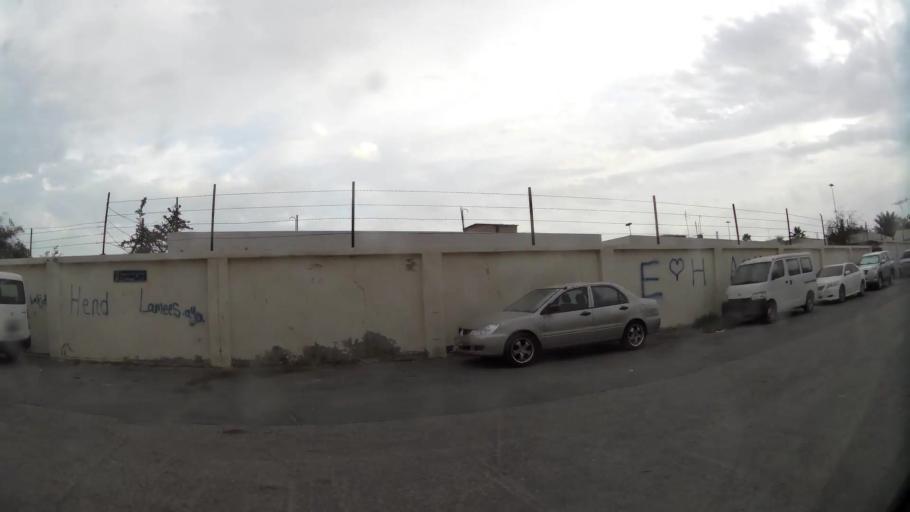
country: QA
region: Baladiyat ad Dawhah
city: Doha
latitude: 25.2696
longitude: 51.4952
